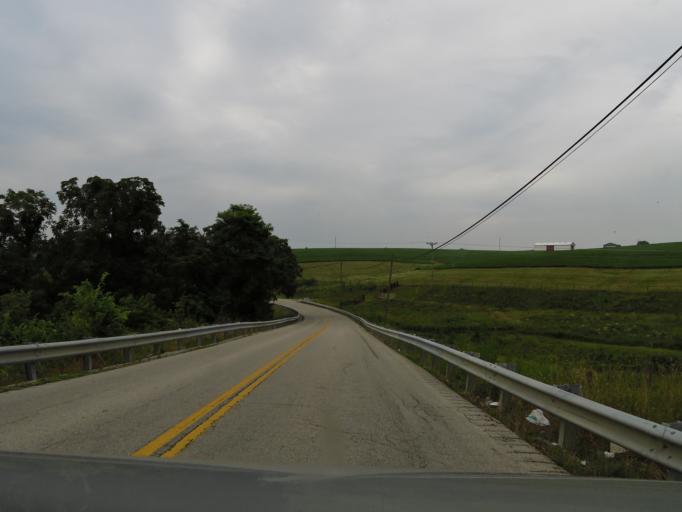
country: US
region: Kentucky
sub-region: Robertson County
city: Mount Olivet
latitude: 38.5210
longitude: -83.8984
